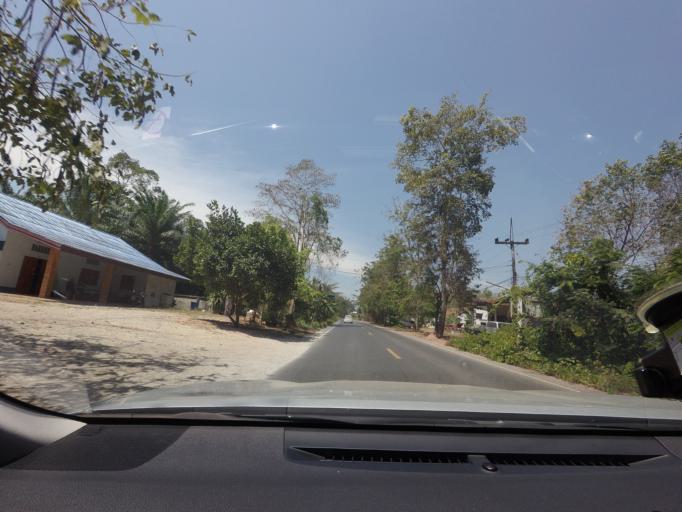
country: TH
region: Surat Thani
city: Tha Chang
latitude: 9.2671
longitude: 99.1553
